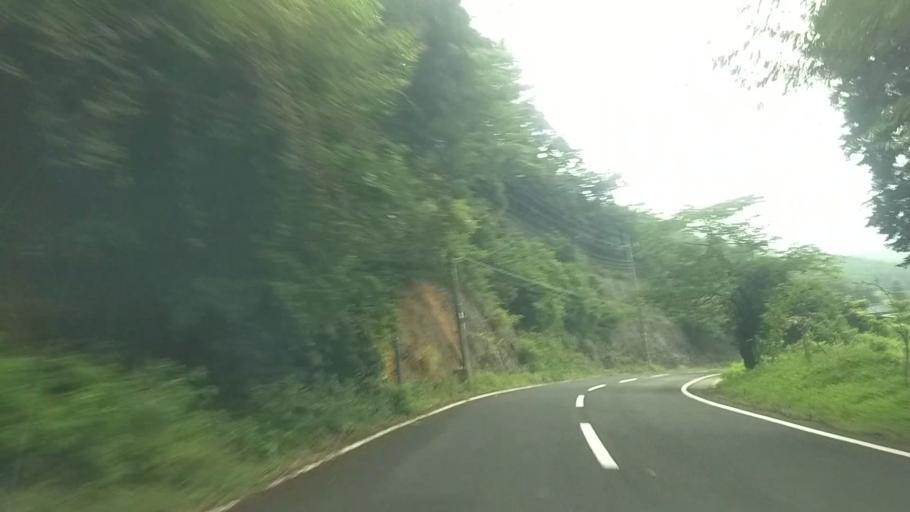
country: JP
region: Chiba
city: Kawaguchi
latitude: 35.1721
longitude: 140.1342
